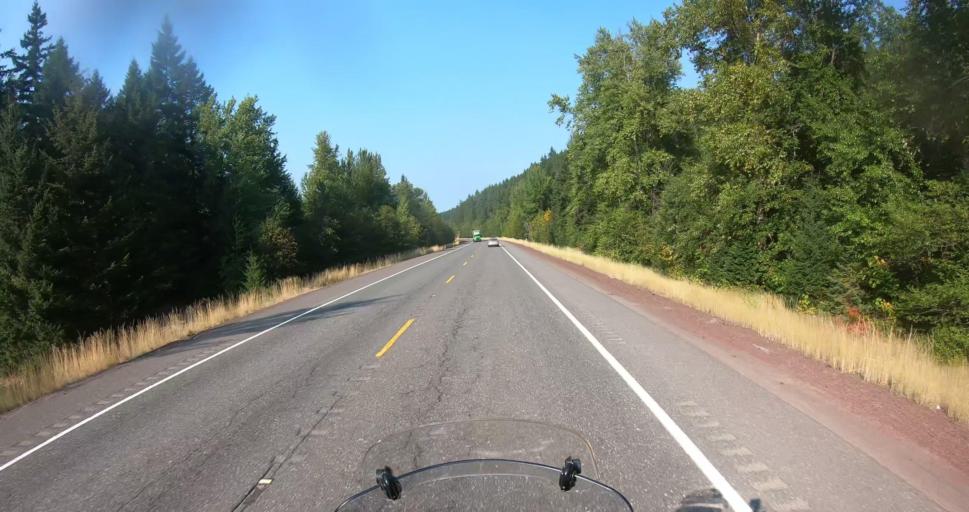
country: US
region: Oregon
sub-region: Hood River County
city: Odell
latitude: 45.4727
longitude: -121.5617
